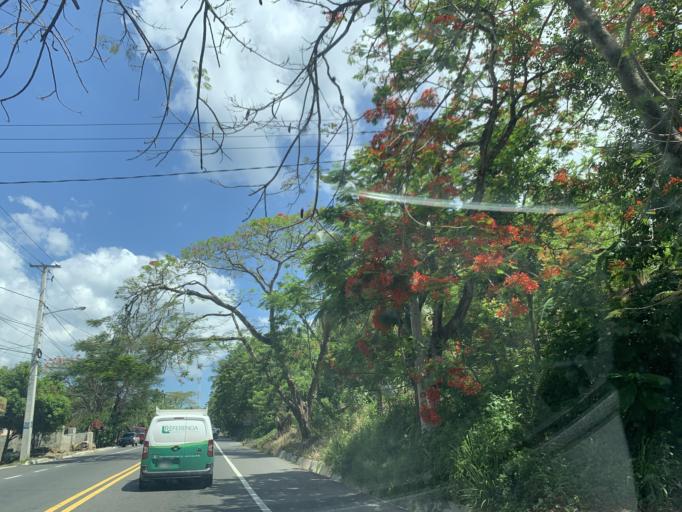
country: DO
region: Puerto Plata
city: Altamira
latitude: 19.6816
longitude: -70.8377
